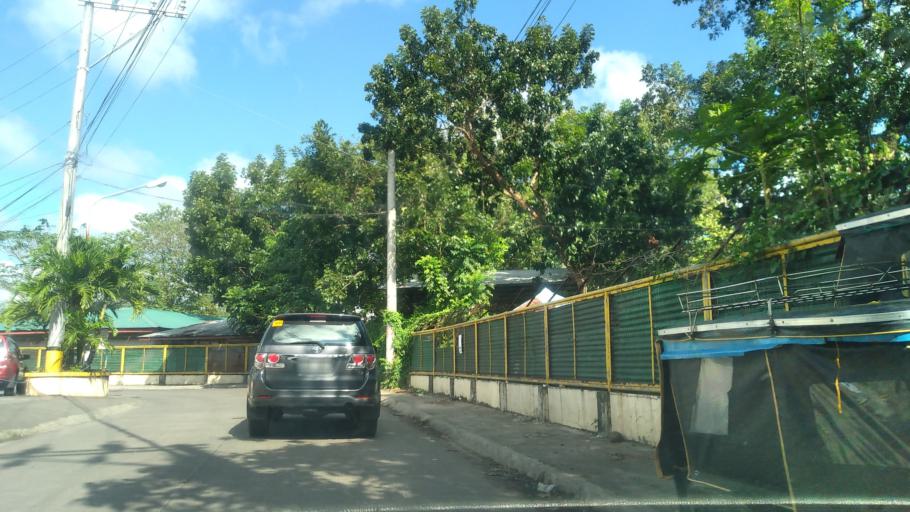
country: PH
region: Calabarzon
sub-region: Province of Quezon
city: Lucena
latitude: 13.9412
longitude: 121.6118
